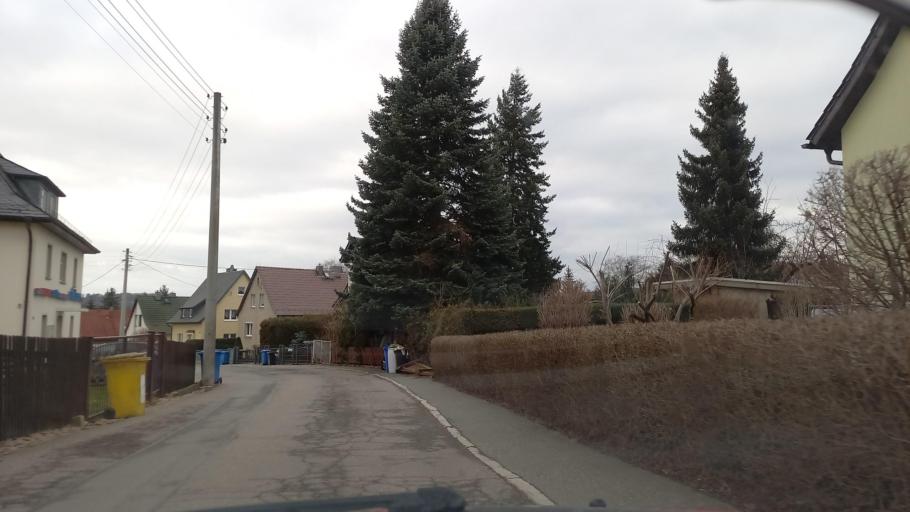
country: DE
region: Saxony
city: Wilkau-Hasslau
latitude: 50.6797
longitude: 12.5116
